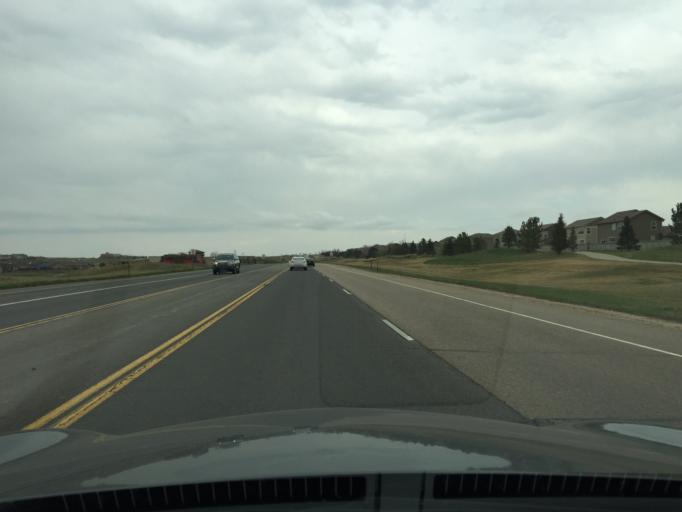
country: US
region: Colorado
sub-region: Boulder County
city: Erie
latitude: 40.0003
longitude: -105.0257
